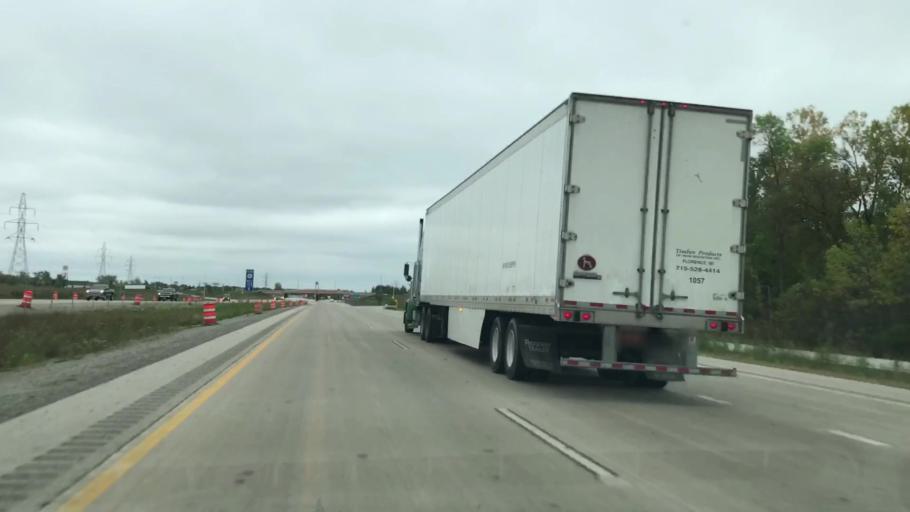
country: US
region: Wisconsin
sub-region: Brown County
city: Suamico
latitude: 44.5976
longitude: -88.0497
